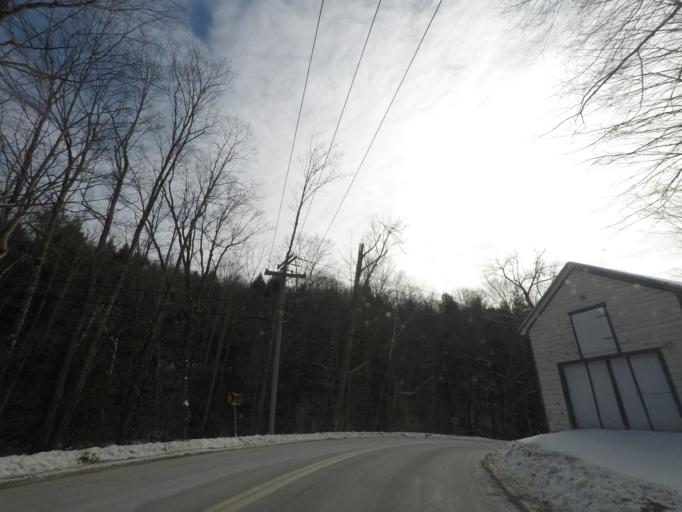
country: US
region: New York
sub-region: Rensselaer County
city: Averill Park
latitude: 42.5568
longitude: -73.5059
